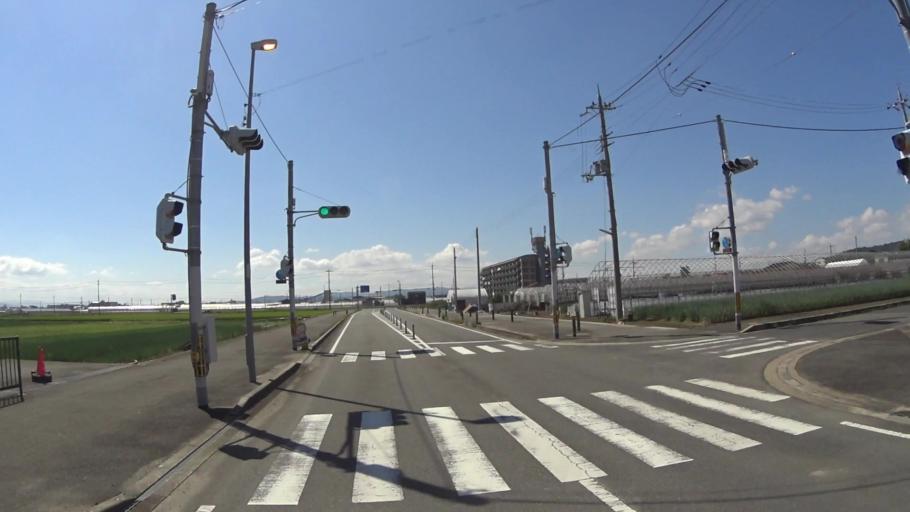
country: JP
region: Kyoto
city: Yawata
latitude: 34.8943
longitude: 135.7244
